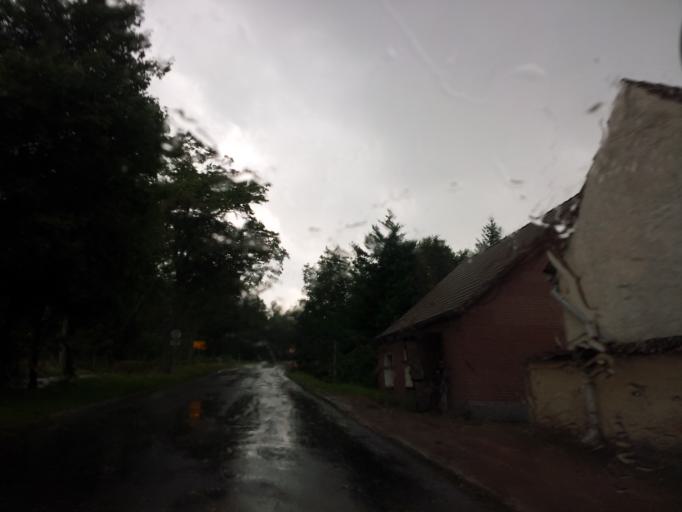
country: DE
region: Brandenburg
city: Wollin
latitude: 52.2798
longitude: 12.4678
